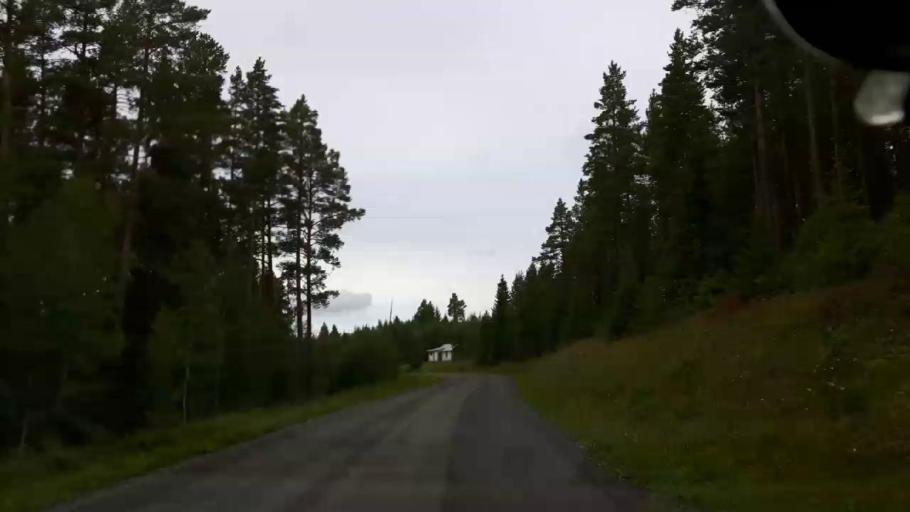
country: SE
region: Jaemtland
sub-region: Krokoms Kommun
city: Krokom
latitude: 63.3040
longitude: 14.3456
